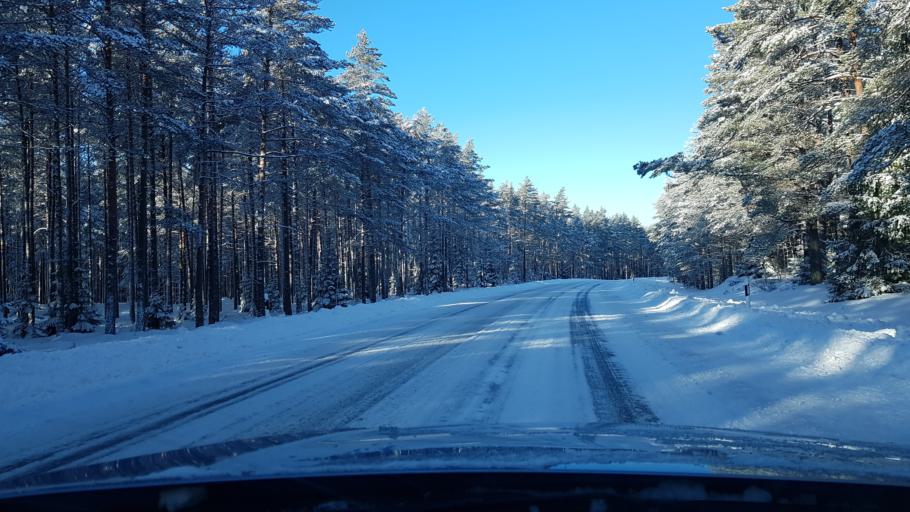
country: EE
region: Hiiumaa
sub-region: Kaerdla linn
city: Kardla
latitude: 58.9277
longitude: 22.7856
